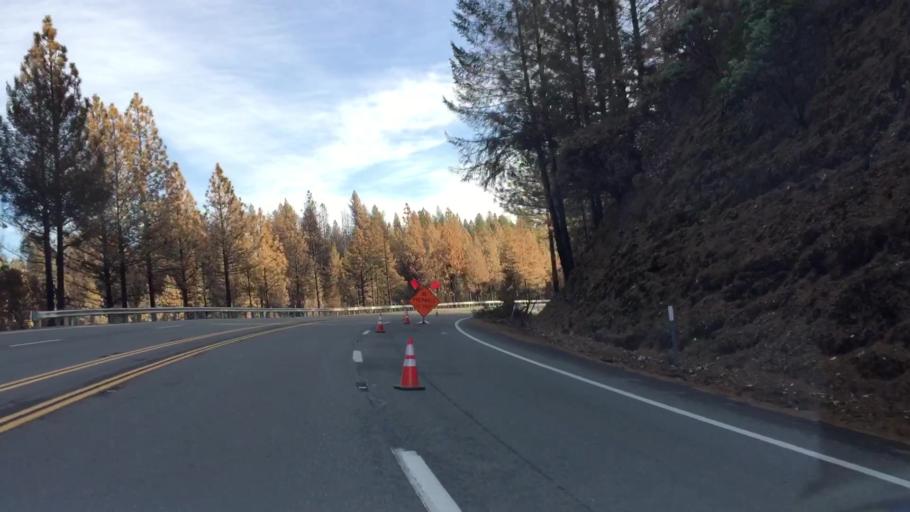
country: US
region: California
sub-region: Butte County
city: Paradise
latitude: 39.7098
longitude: -121.5293
